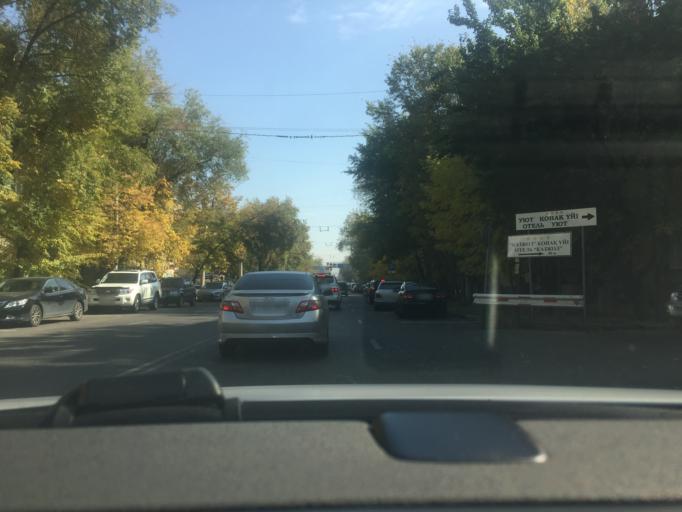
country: KZ
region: Almaty Qalasy
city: Almaty
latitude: 43.2612
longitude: 76.9333
